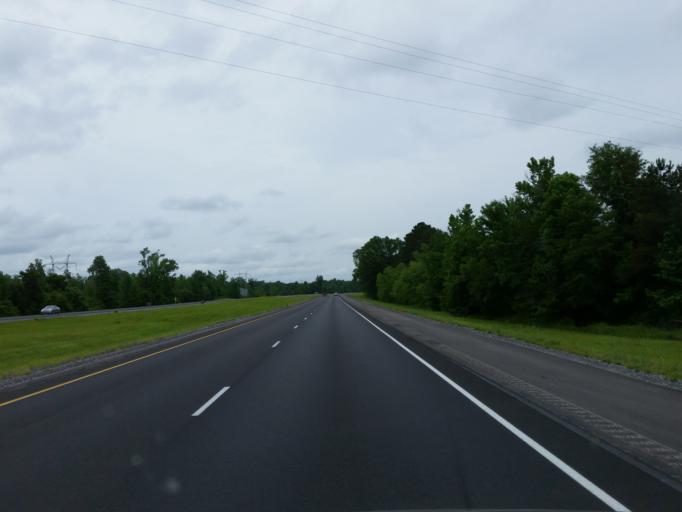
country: US
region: Mississippi
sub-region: Jones County
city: Sharon
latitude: 31.9175
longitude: -89.0055
